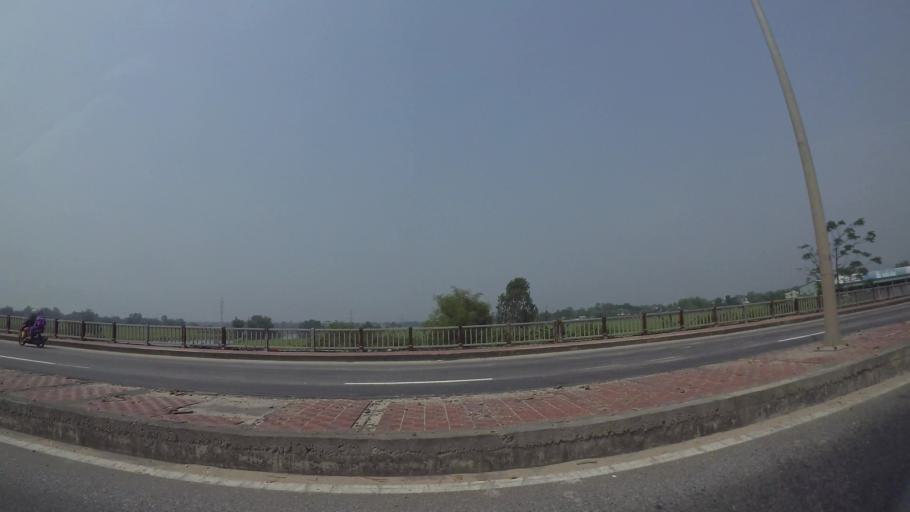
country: VN
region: Da Nang
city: Cam Le
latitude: 15.9725
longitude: 108.2088
